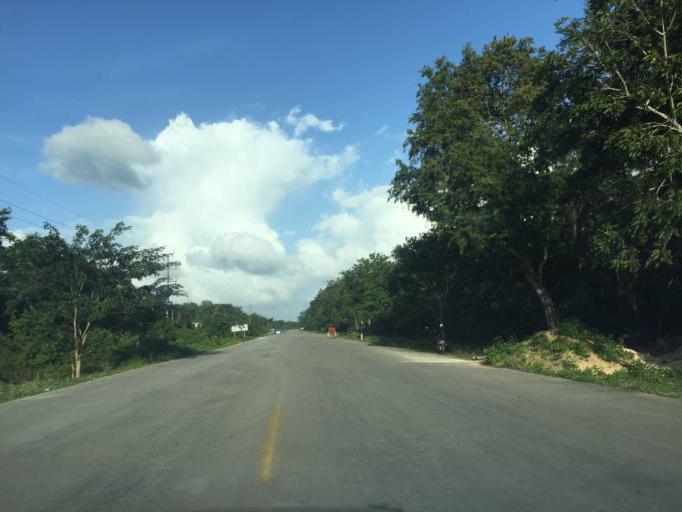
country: MX
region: Quintana Roo
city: Coba
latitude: 20.5017
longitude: -87.7291
